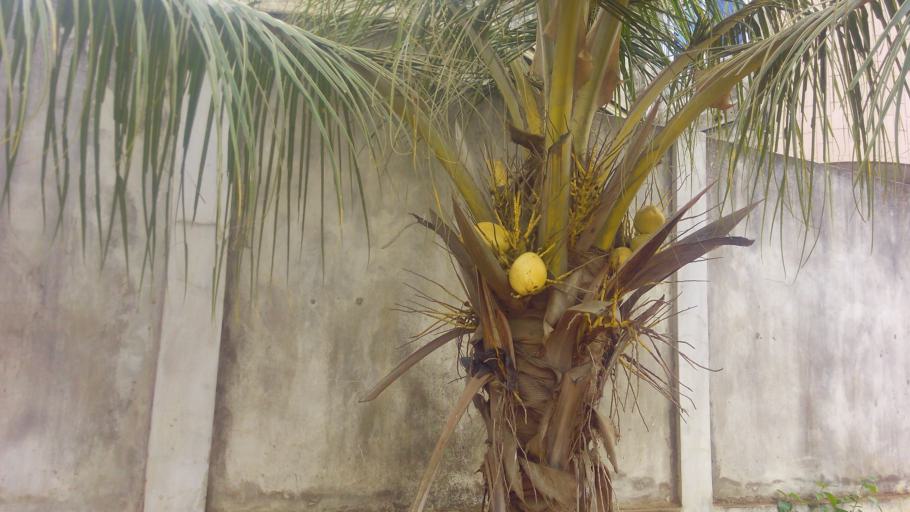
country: BJ
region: Atlantique
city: Abomey-Calavi
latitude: 6.4468
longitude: 2.3429
